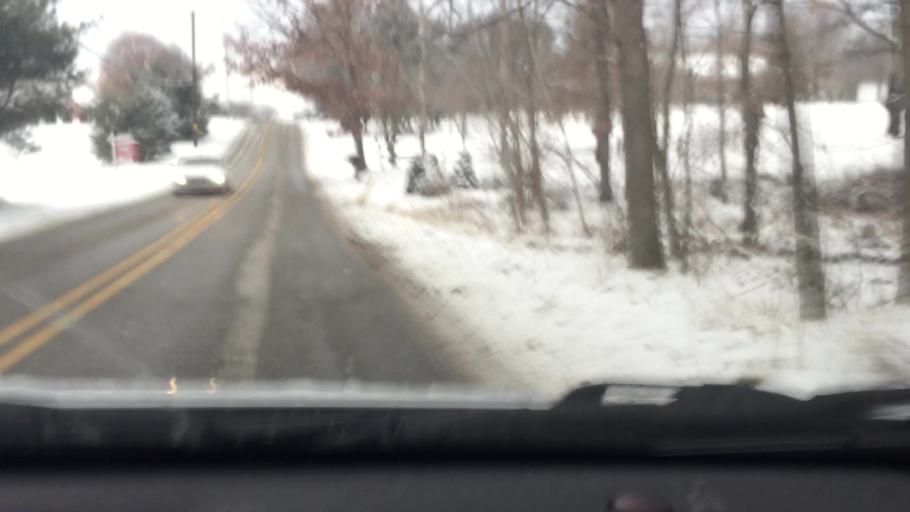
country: US
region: Pennsylvania
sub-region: Butler County
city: Fernway
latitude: 40.7247
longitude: -80.1162
